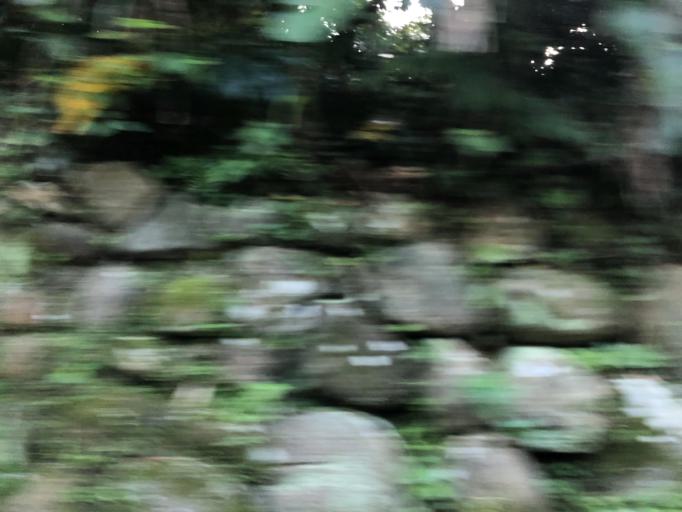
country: TW
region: Taiwan
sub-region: Keelung
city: Keelung
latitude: 25.1937
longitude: 121.6440
